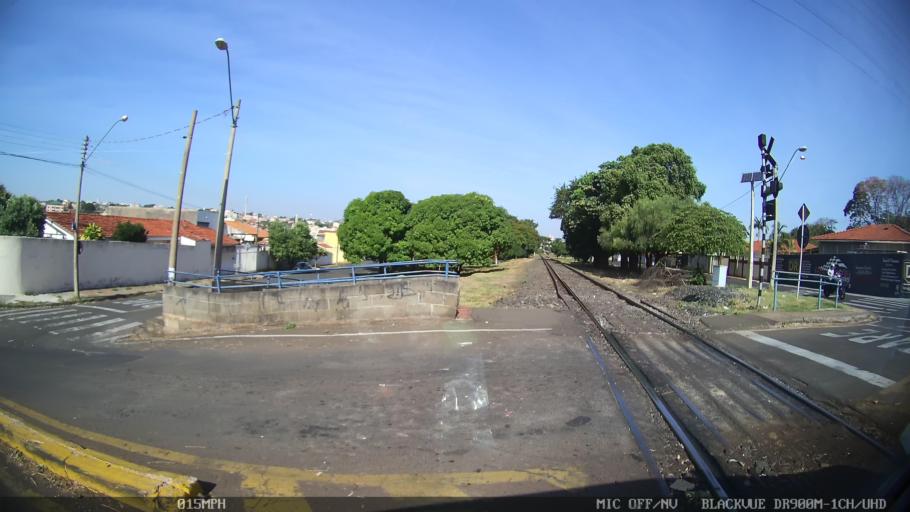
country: BR
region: Sao Paulo
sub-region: Sao Jose Do Rio Preto
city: Sao Jose do Rio Preto
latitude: -20.7910
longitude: -49.3794
